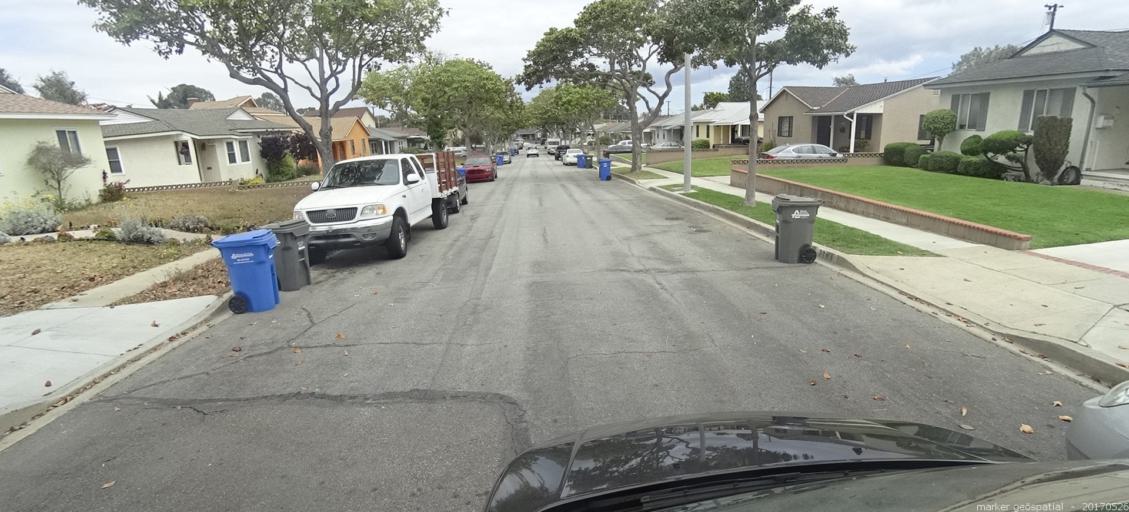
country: US
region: California
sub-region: Los Angeles County
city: Lawndale
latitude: 33.8627
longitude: -118.3609
